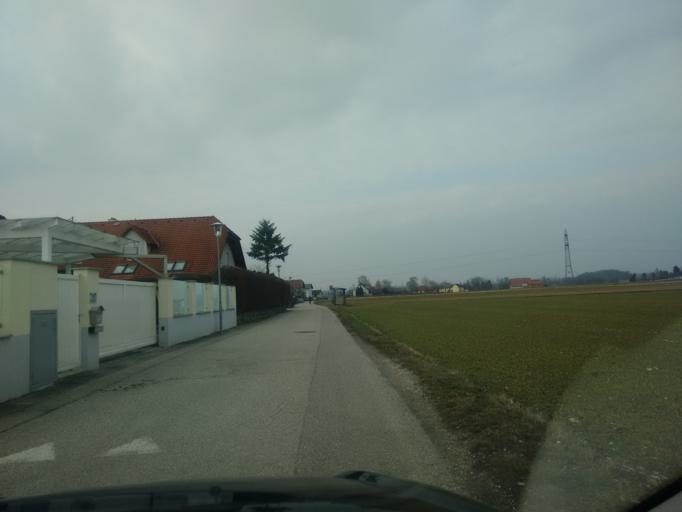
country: AT
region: Upper Austria
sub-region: Wels-Land
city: Marchtrenk
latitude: 48.2022
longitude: 14.1475
